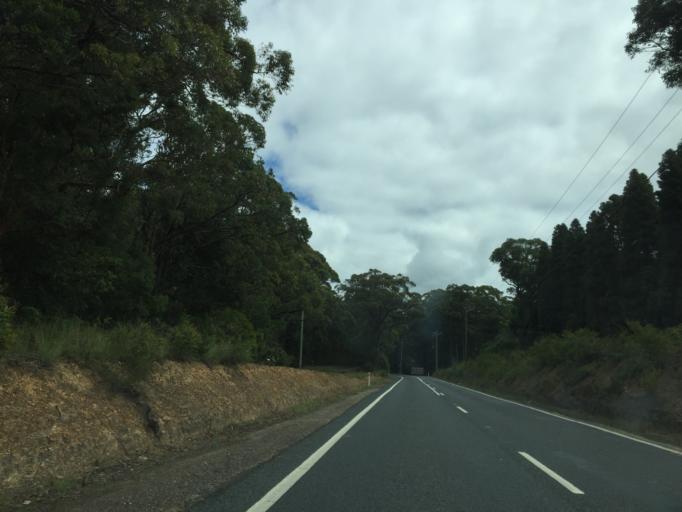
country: AU
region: New South Wales
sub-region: Hawkesbury
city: Richmond
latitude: -33.5175
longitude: 150.6137
